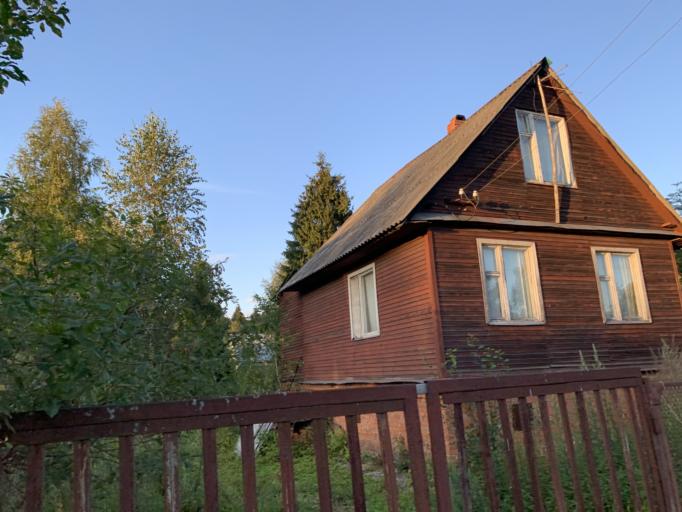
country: RU
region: Moskovskaya
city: Podosinki
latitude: 56.1775
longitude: 37.5784
